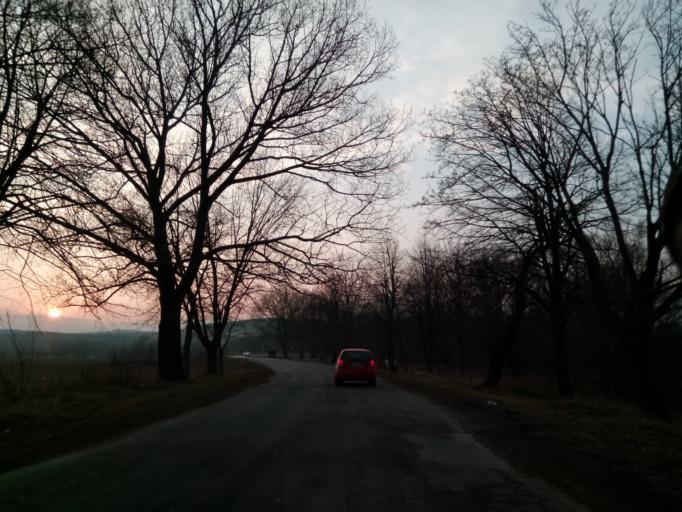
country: HU
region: Borsod-Abauj-Zemplen
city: Gonc
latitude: 48.4968
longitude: 21.2347
